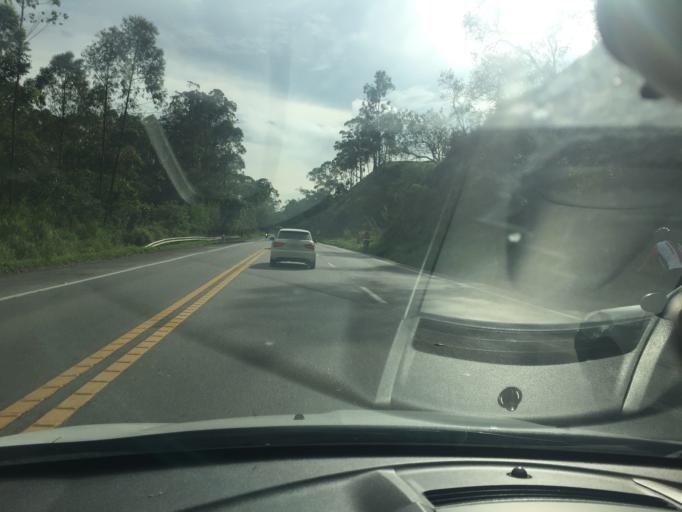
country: BR
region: Sao Paulo
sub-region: Campo Limpo Paulista
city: Campo Limpo Paulista
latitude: -23.1701
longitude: -46.7670
